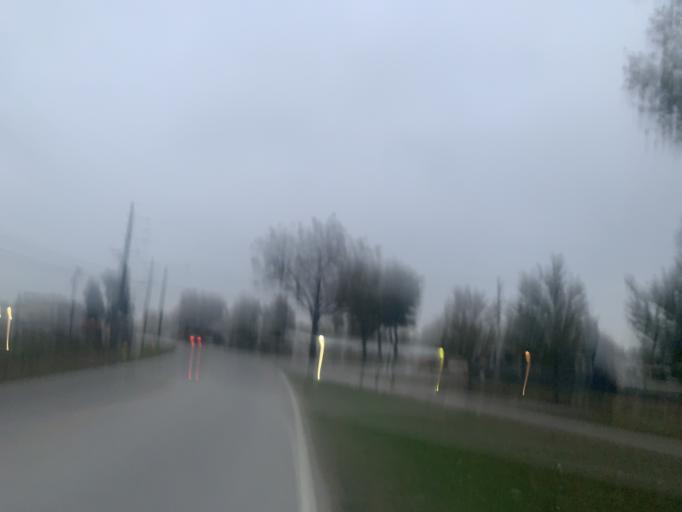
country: US
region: Kentucky
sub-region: Jefferson County
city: Shively
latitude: 38.2156
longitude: -85.8072
